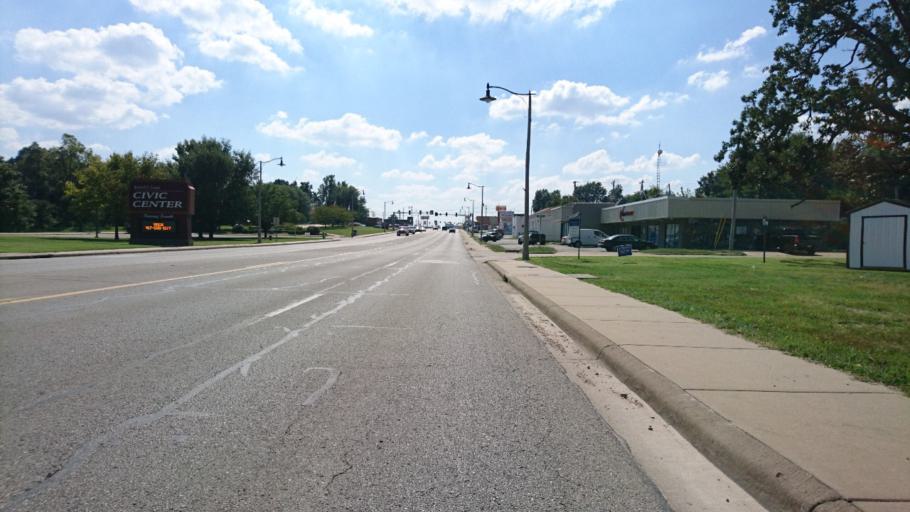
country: US
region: Missouri
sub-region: Laclede County
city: Lebanon
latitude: 37.6794
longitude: -92.6548
